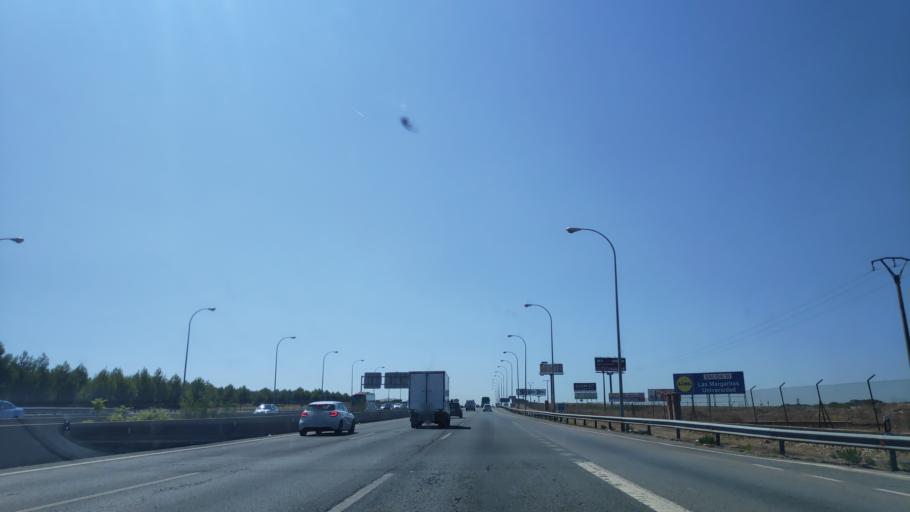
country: ES
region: Madrid
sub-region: Provincia de Madrid
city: Villaverde
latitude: 40.3591
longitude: -3.7216
